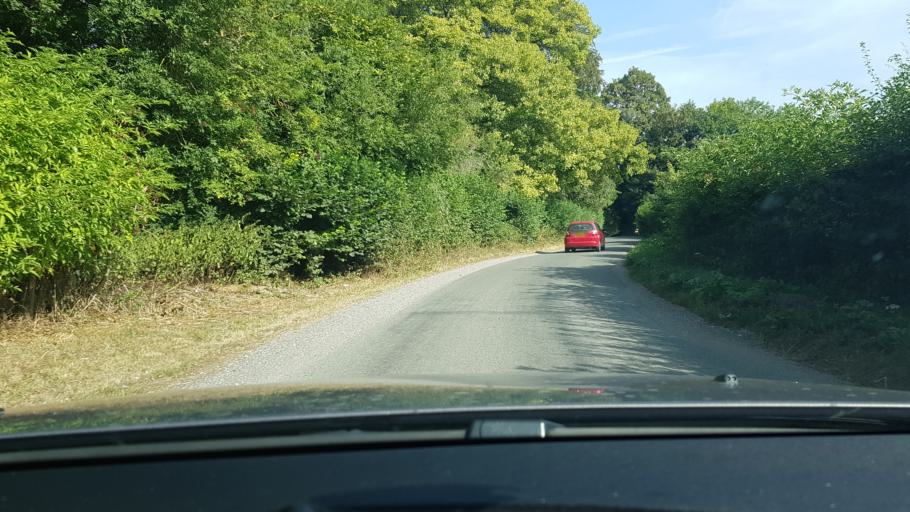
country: GB
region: England
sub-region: Wiltshire
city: Ramsbury
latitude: 51.4566
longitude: -1.5959
